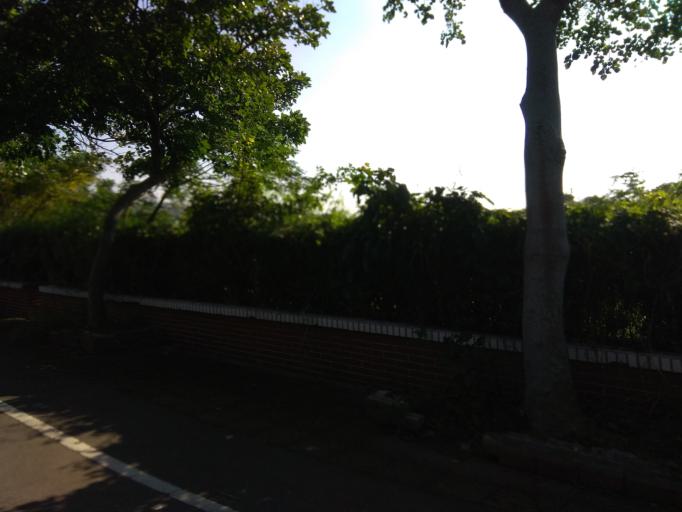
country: TW
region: Taiwan
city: Taoyuan City
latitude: 25.0509
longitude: 121.2283
